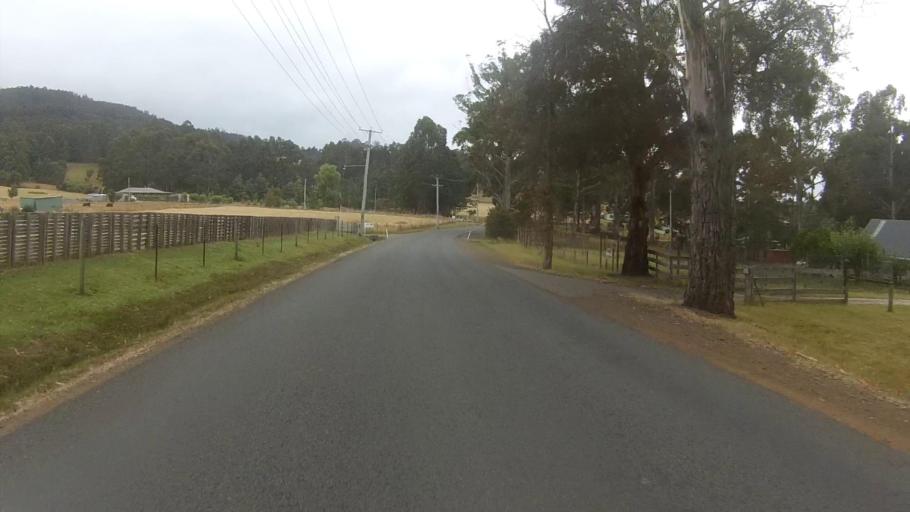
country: AU
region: Tasmania
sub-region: Kingborough
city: Margate
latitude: -42.9606
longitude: 147.2203
